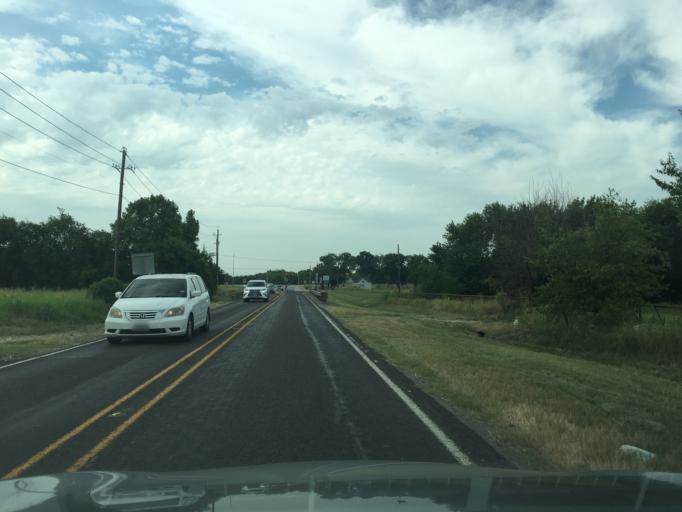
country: US
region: Texas
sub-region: Collin County
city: Parker
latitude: 33.0579
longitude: -96.6189
